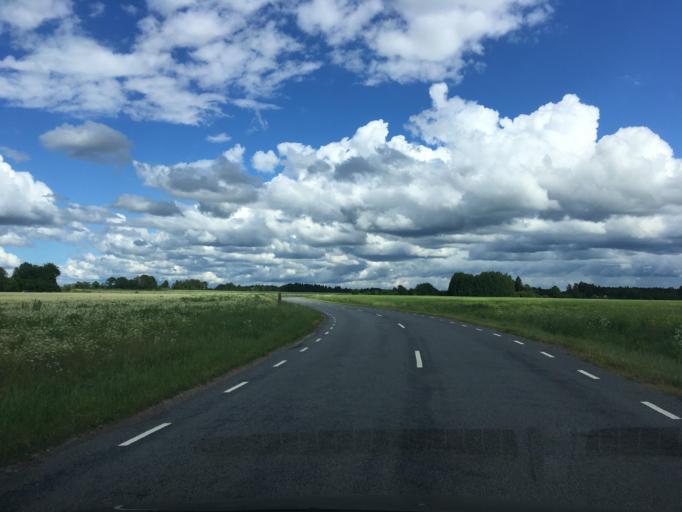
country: EE
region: Paernumaa
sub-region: Halinga vald
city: Parnu-Jaagupi
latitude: 58.6217
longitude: 24.3995
